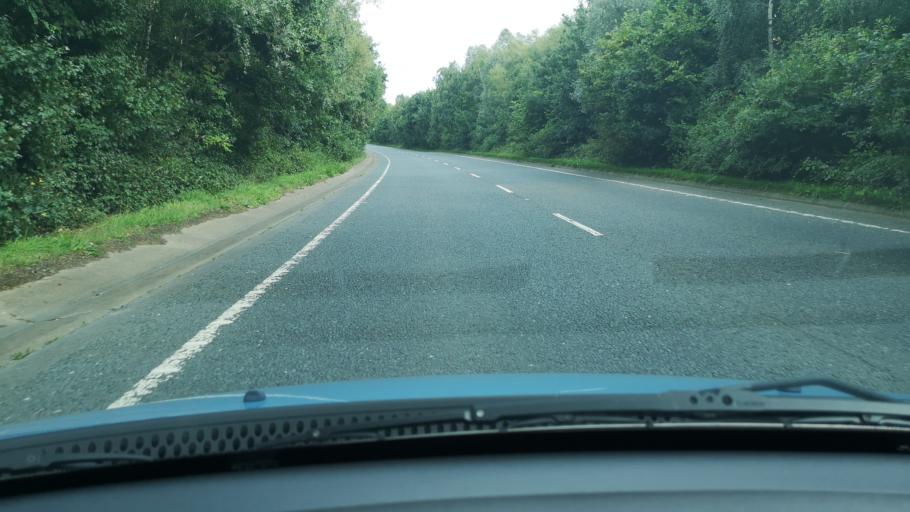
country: GB
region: England
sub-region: City and Borough of Wakefield
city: Hemsworth
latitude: 53.6013
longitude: -1.3687
